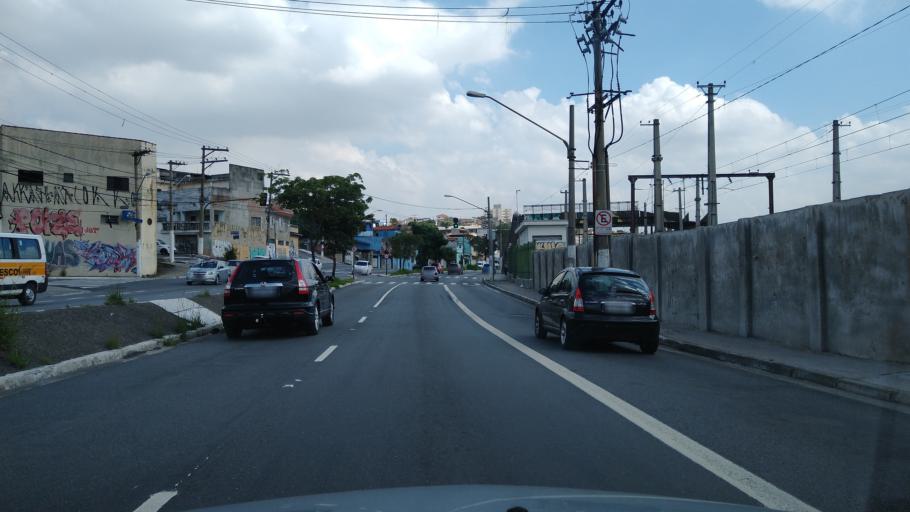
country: BR
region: Sao Paulo
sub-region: Guarulhos
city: Guarulhos
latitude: -23.5080
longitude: -46.5428
